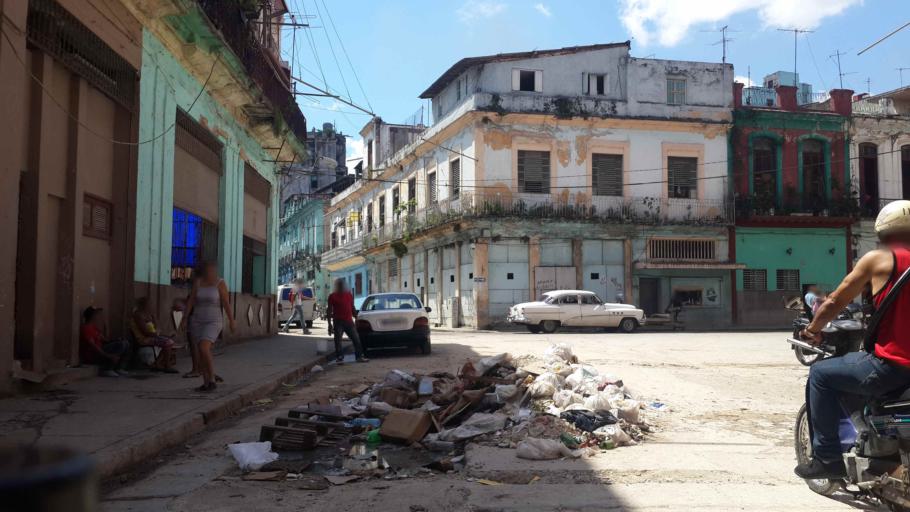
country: CU
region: La Habana
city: Centro Habana
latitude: 23.1385
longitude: -82.3600
